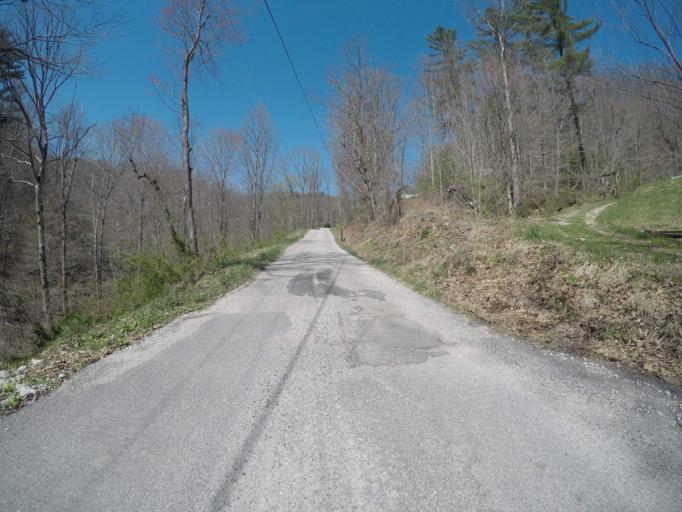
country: US
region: West Virginia
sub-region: Kanawha County
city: Charleston
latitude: 38.4072
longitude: -81.5890
